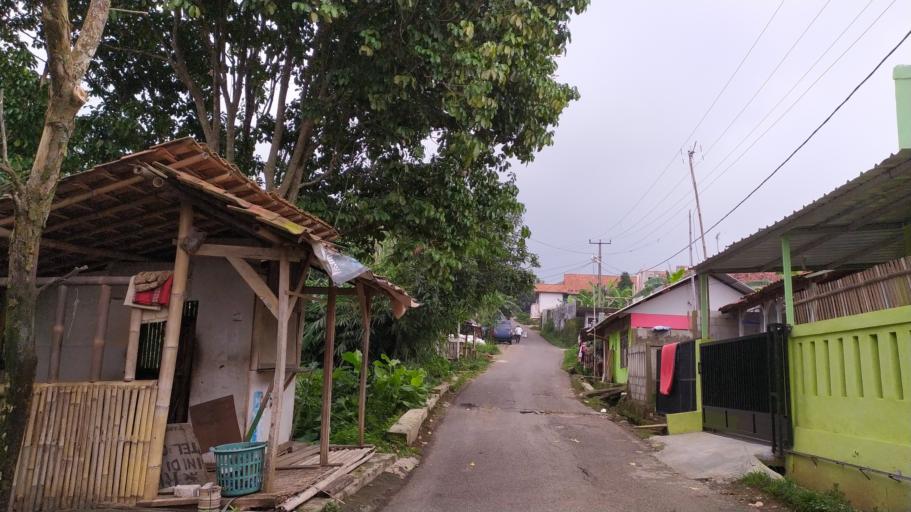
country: ID
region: West Java
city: Ciampea
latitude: -6.6366
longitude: 106.7072
